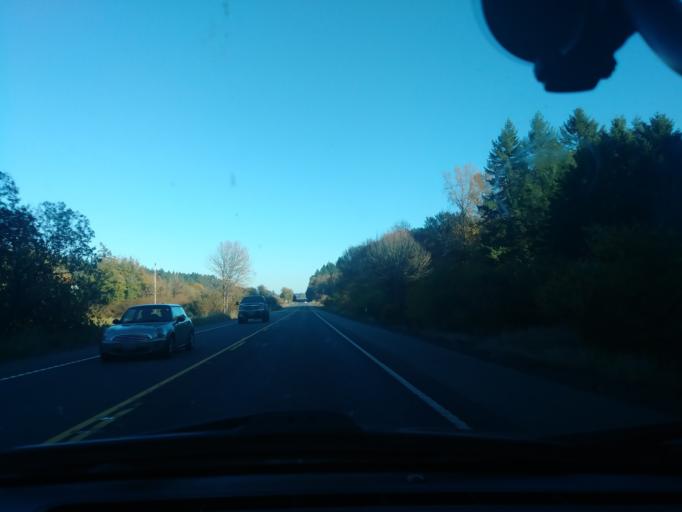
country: US
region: Oregon
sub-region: Washington County
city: Banks
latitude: 45.6154
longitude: -123.1880
